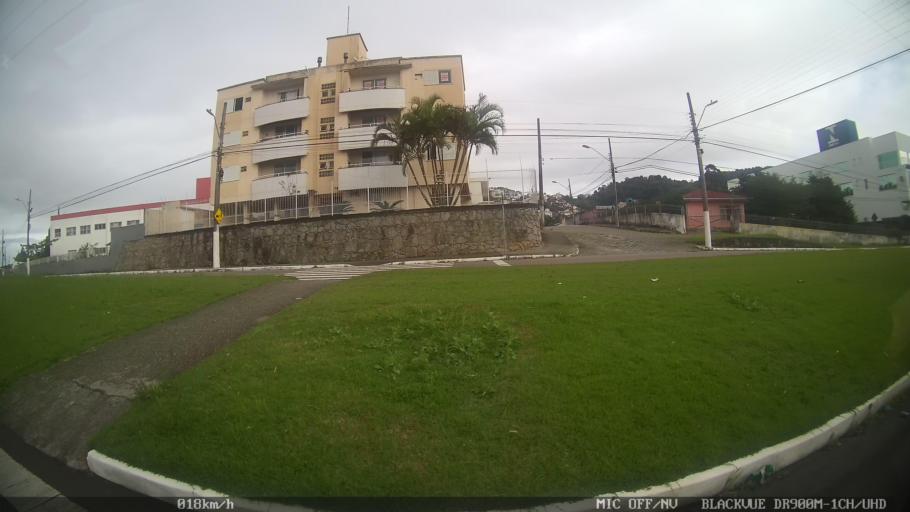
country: BR
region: Santa Catarina
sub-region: Sao Jose
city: Campinas
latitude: -27.5793
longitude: -48.6220
